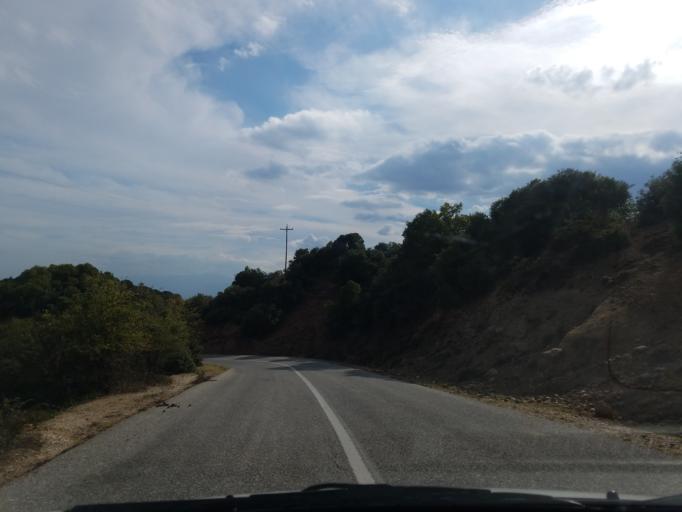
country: GR
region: Thessaly
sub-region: Trikala
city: Kastraki
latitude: 39.7278
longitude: 21.6483
